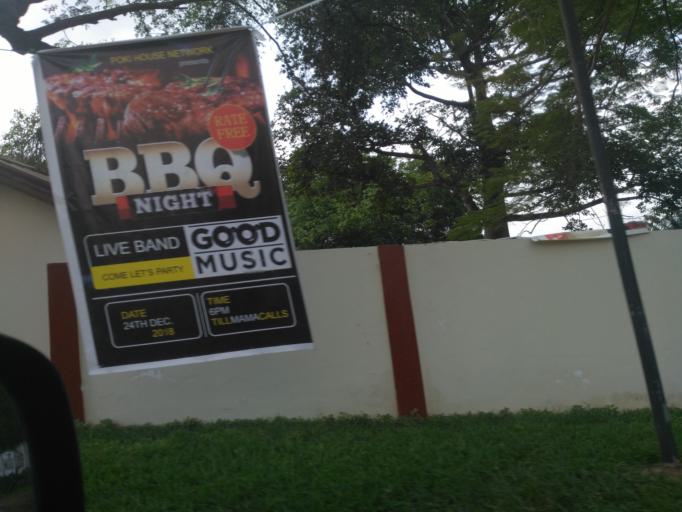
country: GH
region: Greater Accra
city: Accra
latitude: 5.6053
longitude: -0.1841
